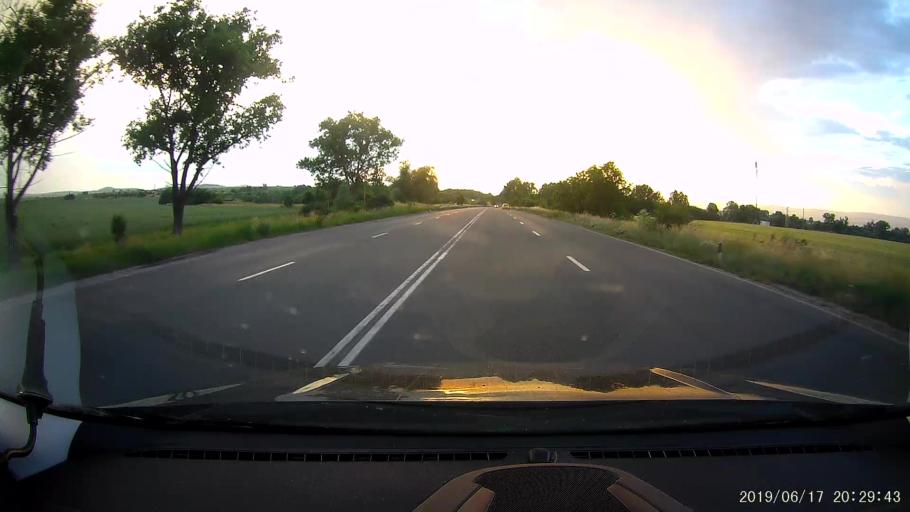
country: BG
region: Sofiya
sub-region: Obshtina Bozhurishte
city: Bozhurishte
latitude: 42.7889
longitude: 23.1565
